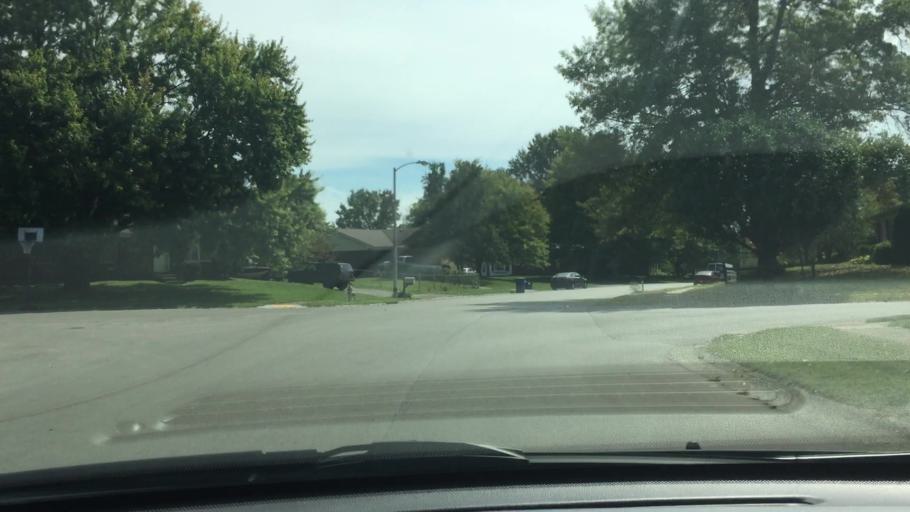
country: US
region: Kentucky
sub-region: Fayette County
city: Monticello
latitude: 37.9729
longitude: -84.5269
